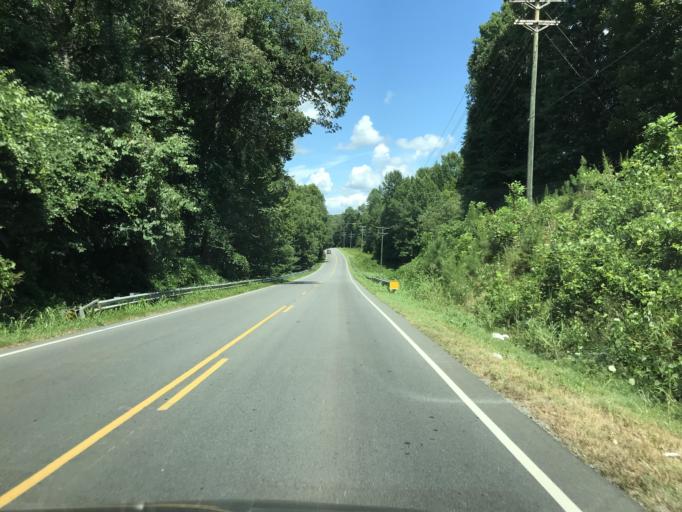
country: US
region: North Carolina
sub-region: Lincoln County
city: Pumpkin Center
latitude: 35.5061
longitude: -81.1684
